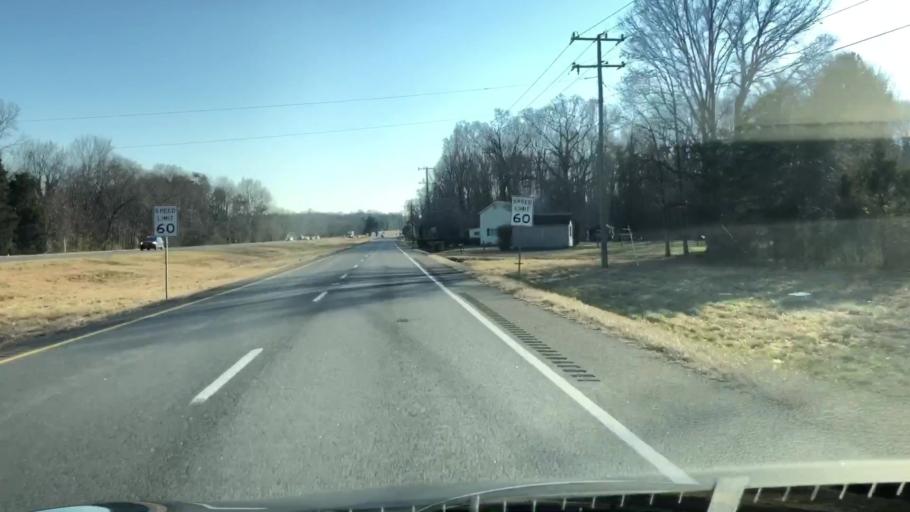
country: US
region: Virginia
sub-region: Fauquier County
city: Bealeton
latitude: 38.6071
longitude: -77.8005
